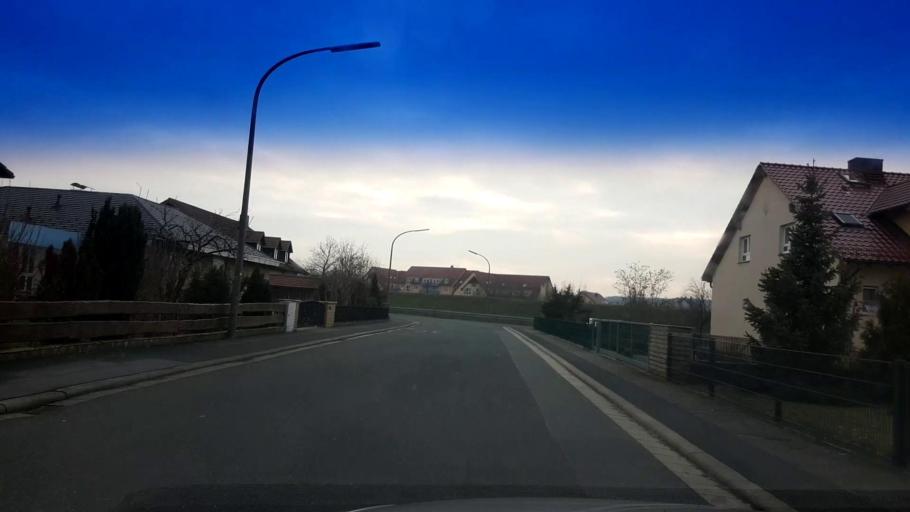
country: DE
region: Bavaria
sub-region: Upper Franconia
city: Hirschaid
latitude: 49.8177
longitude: 10.9838
